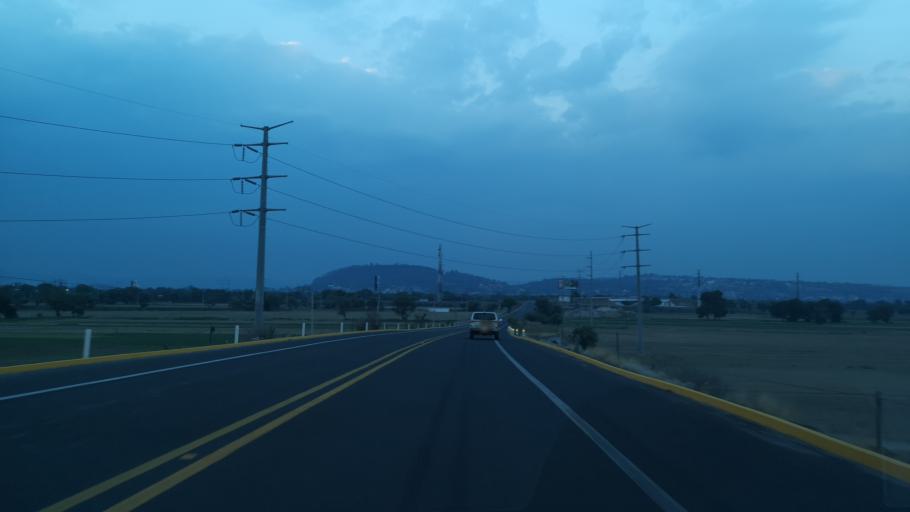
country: MX
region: Puebla
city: Santa Ana Xalmimilulco
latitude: 19.2094
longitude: -98.3601
